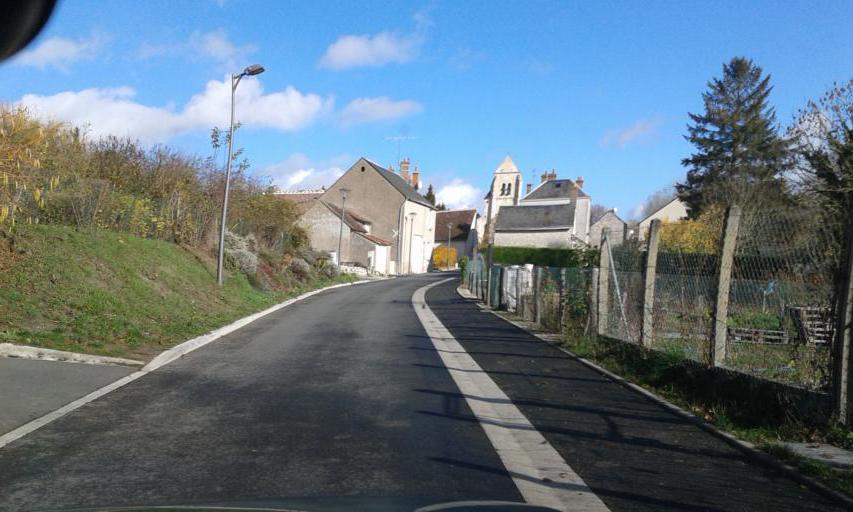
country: FR
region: Centre
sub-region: Departement du Loir-et-Cher
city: Mer
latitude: 47.7077
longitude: 1.5360
